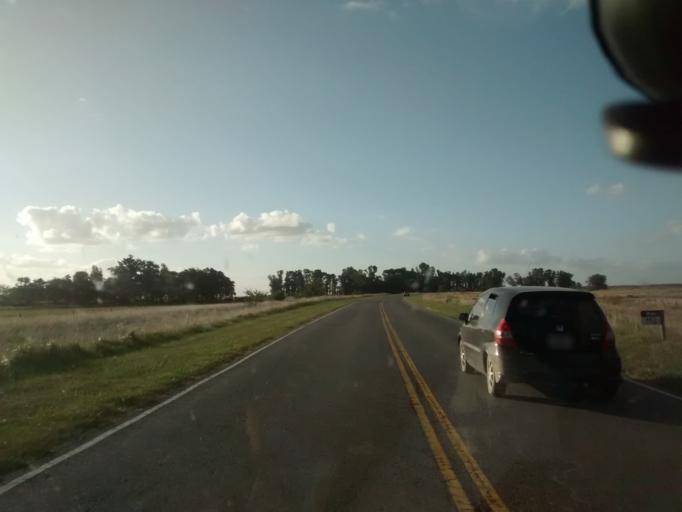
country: AR
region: Buenos Aires
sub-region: Partido de General Belgrano
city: General Belgrano
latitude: -36.1053
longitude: -58.6055
